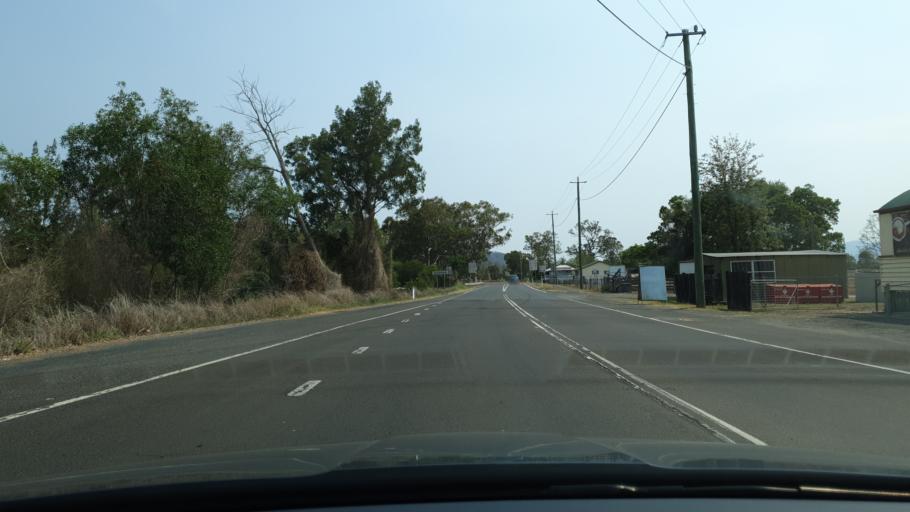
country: AU
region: Queensland
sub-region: Ipswich
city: Deebing Heights
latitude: -28.0043
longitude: 152.6811
